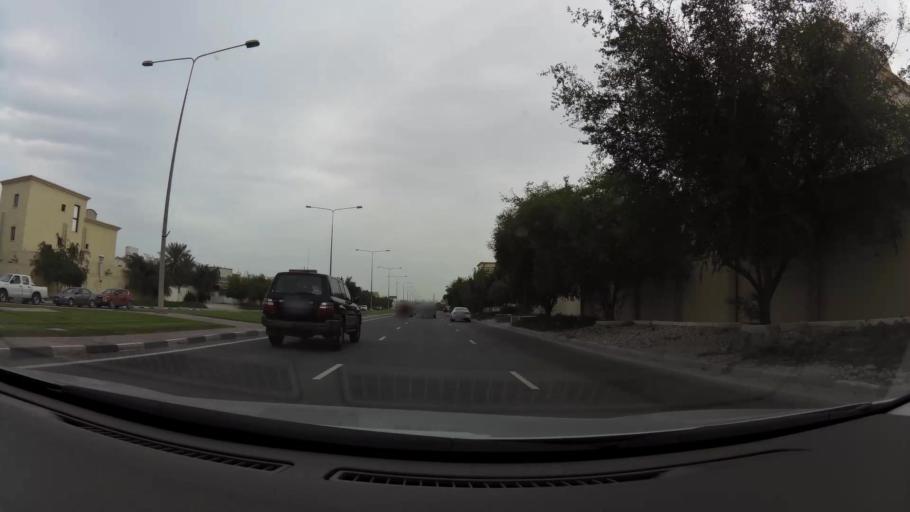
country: QA
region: Baladiyat ad Dawhah
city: Doha
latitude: 25.3405
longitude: 51.5058
